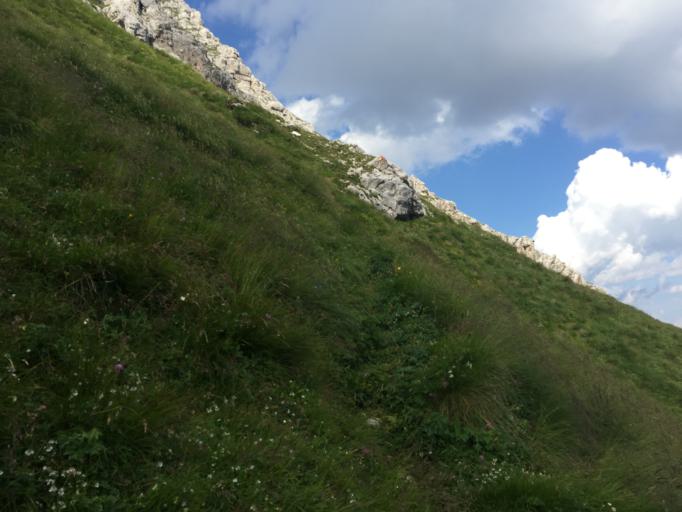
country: IT
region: Friuli Venezia Giulia
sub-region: Provincia di Udine
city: Malborghetto
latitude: 46.4198
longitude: 13.4834
